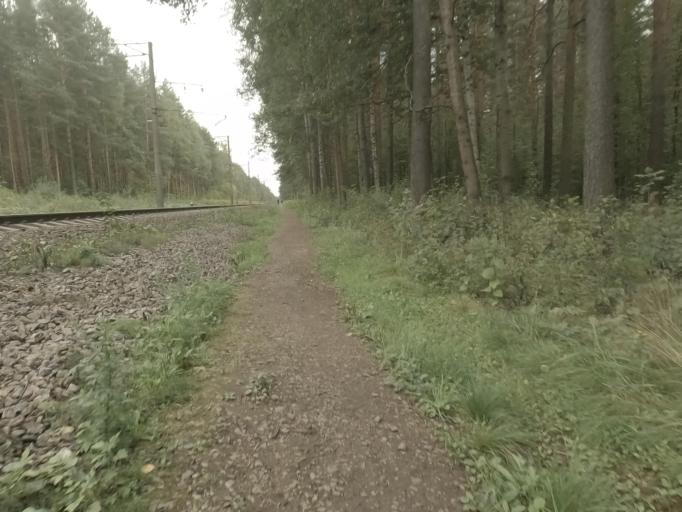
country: RU
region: St.-Petersburg
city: Krasnogvargeisky
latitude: 59.9674
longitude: 30.5123
